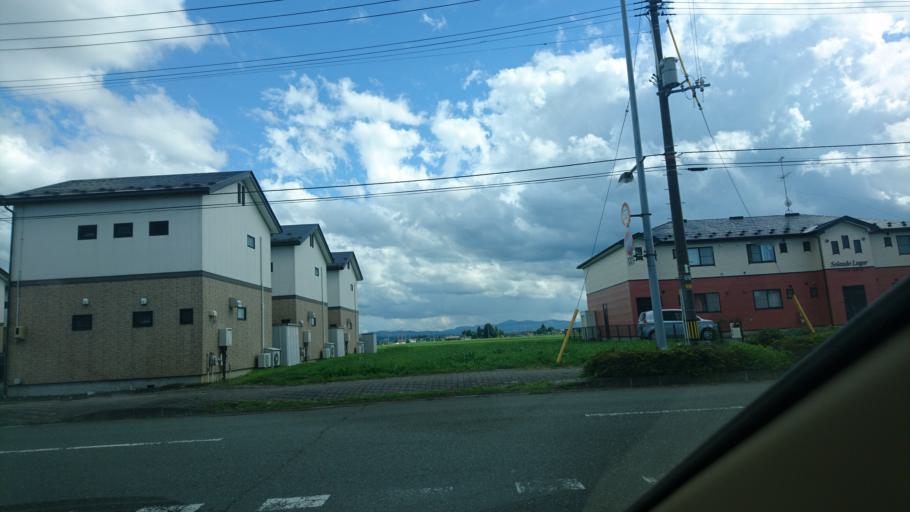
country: JP
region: Iwate
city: Mizusawa
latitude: 39.1825
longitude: 141.1785
